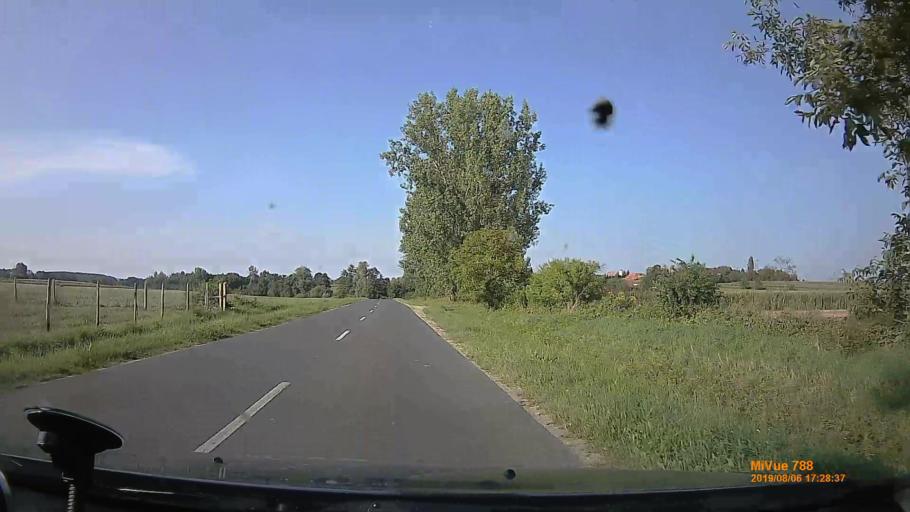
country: HR
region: Medimurska
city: Kotoriba
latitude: 46.3940
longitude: 16.8417
